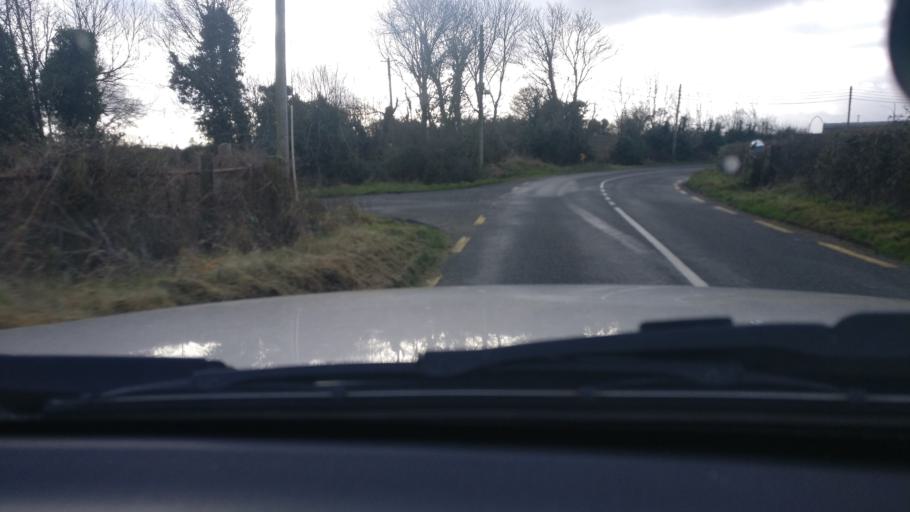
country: IE
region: Connaught
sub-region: County Galway
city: Ballinasloe
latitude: 53.2562
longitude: -8.2588
